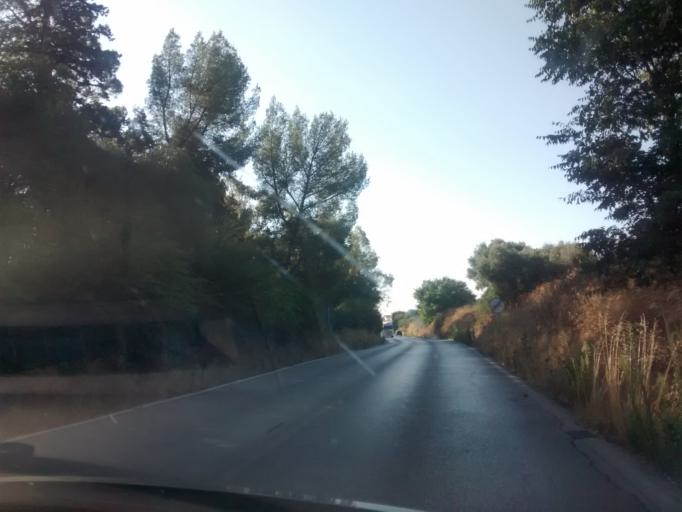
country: ES
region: Andalusia
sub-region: Provincia de Cadiz
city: Jerez de la Frontera
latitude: 36.6699
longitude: -6.1204
